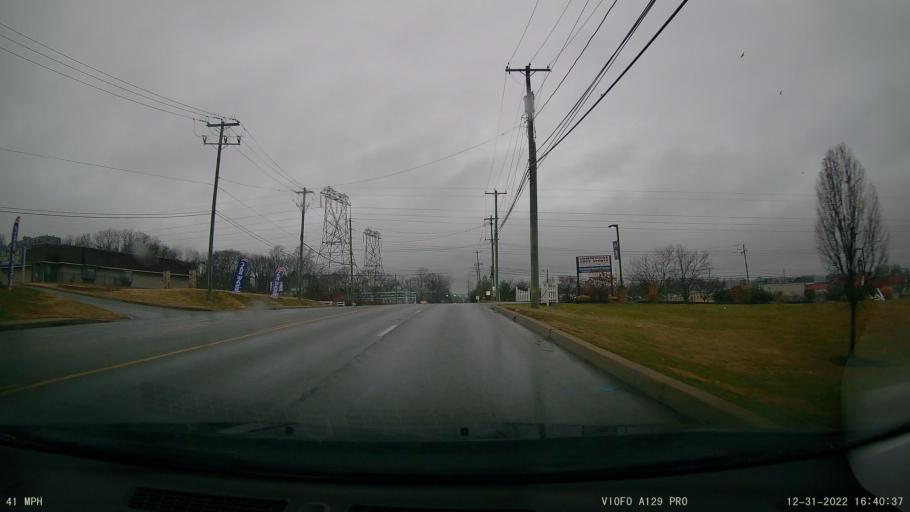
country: US
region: Pennsylvania
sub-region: Montgomery County
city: Bridgeport
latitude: 40.0889
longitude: -75.3583
